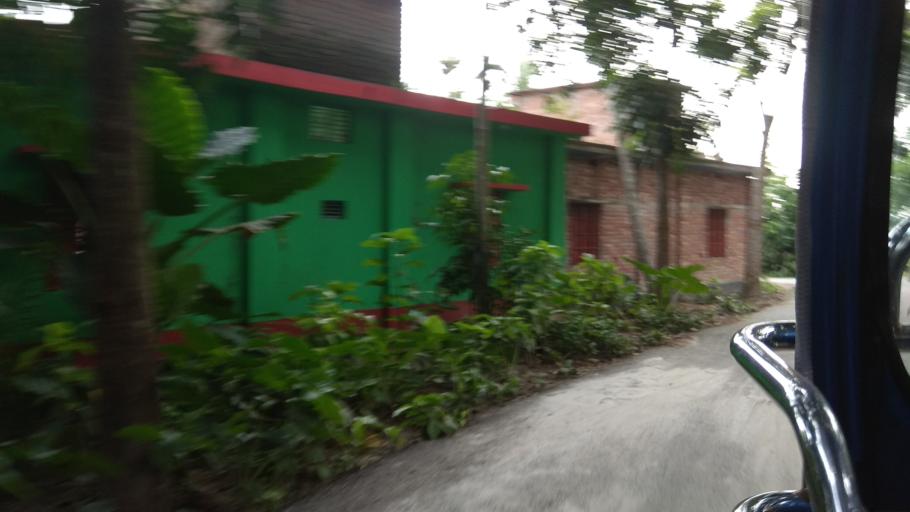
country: BD
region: Khulna
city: Kalia
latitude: 23.0309
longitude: 89.6463
